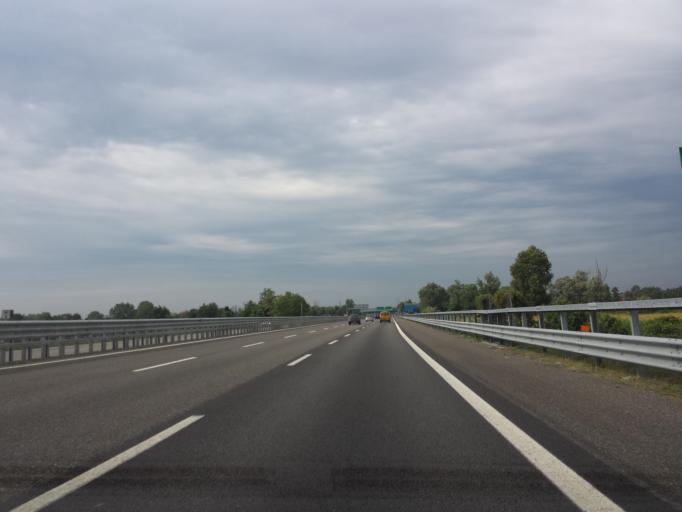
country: IT
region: Lombardy
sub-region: Citta metropolitana di Milano
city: Santa Corinna
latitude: 45.3456
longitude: 9.1039
